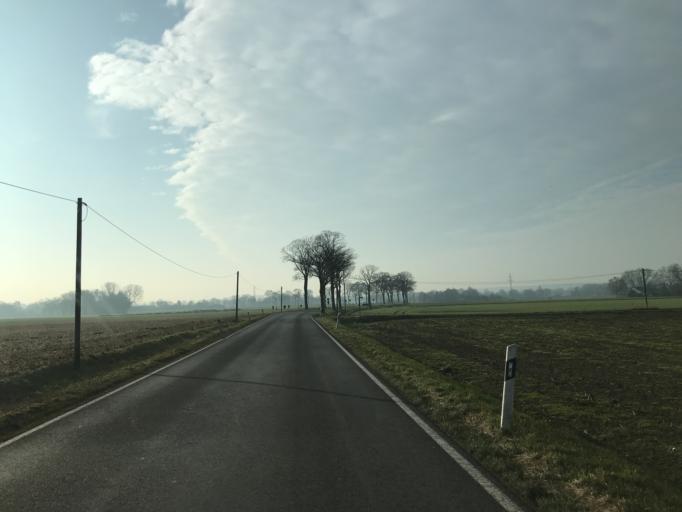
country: DE
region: North Rhine-Westphalia
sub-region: Regierungsbezirk Dusseldorf
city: Viersen
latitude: 51.3018
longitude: 6.3881
